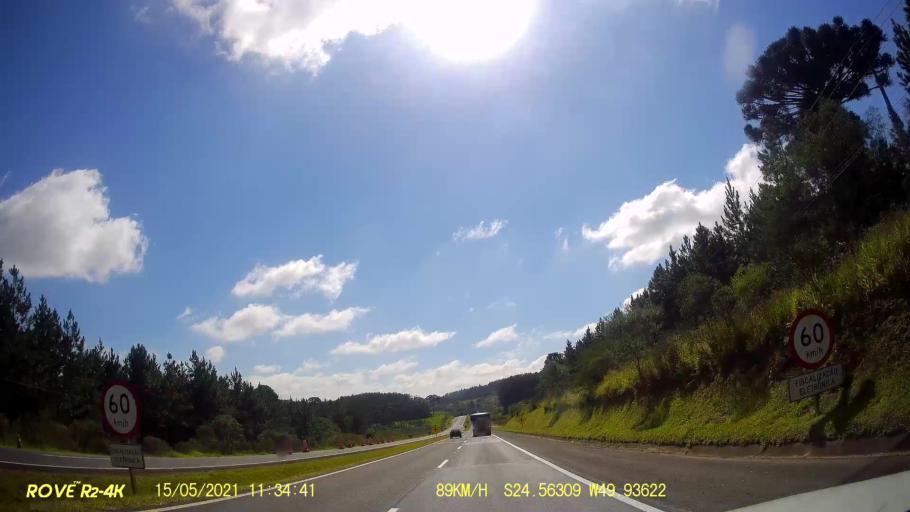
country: BR
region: Parana
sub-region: Pirai Do Sul
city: Pirai do Sul
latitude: -24.5632
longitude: -49.9362
